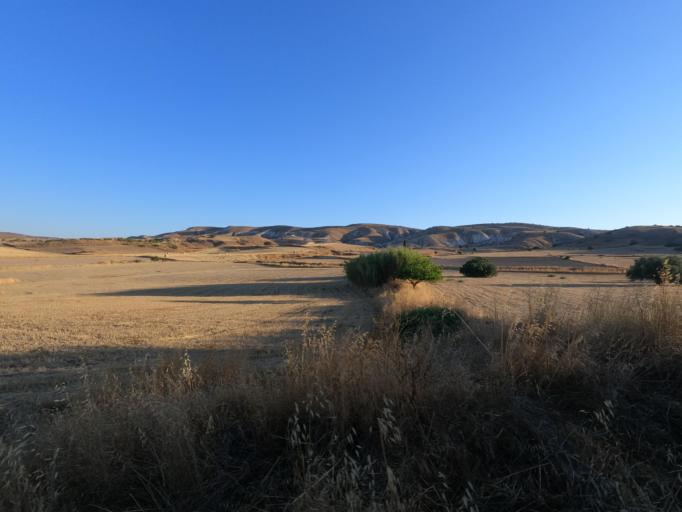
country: CY
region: Larnaka
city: Troulloi
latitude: 35.0298
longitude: 33.6407
